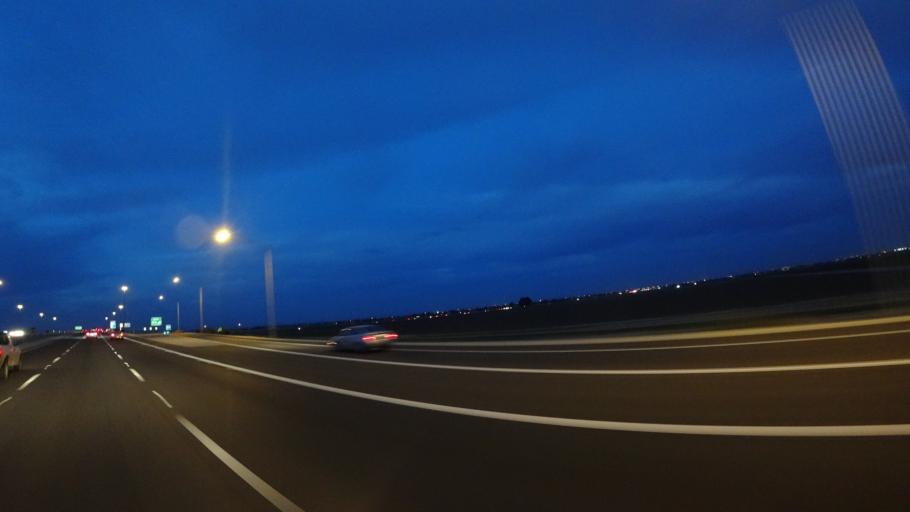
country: US
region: Arizona
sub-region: Maricopa County
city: Citrus Park
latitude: 33.6054
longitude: -112.4179
